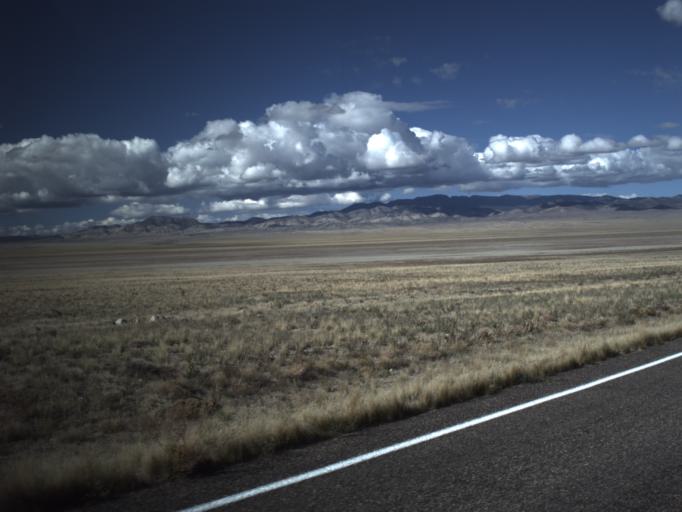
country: US
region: Utah
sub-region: Beaver County
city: Milford
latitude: 38.5167
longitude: -113.6395
